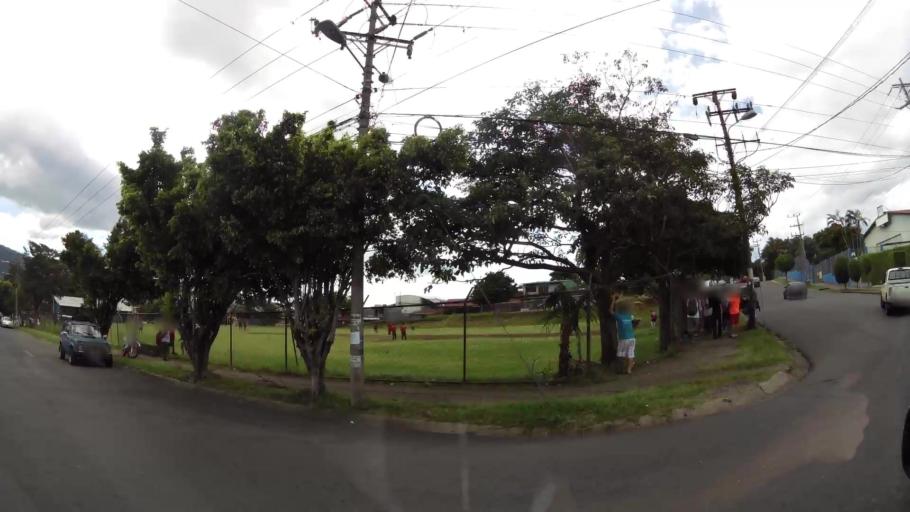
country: CR
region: San Jose
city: San Rafael
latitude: 9.9523
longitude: -84.1475
